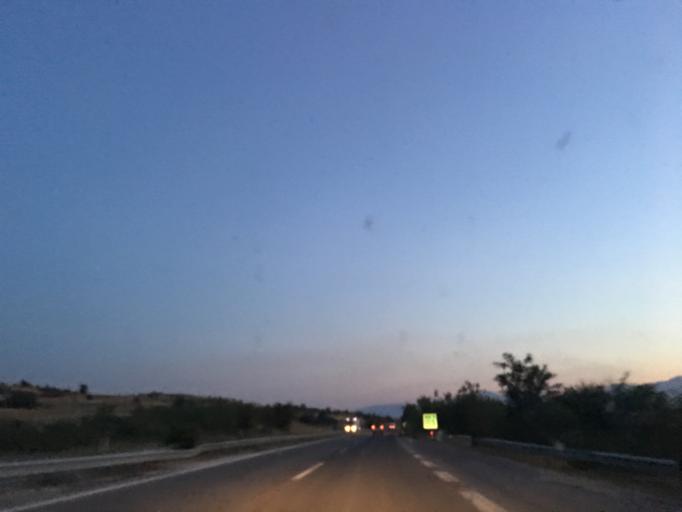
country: MK
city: Miladinovci
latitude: 41.9821
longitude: 21.6532
